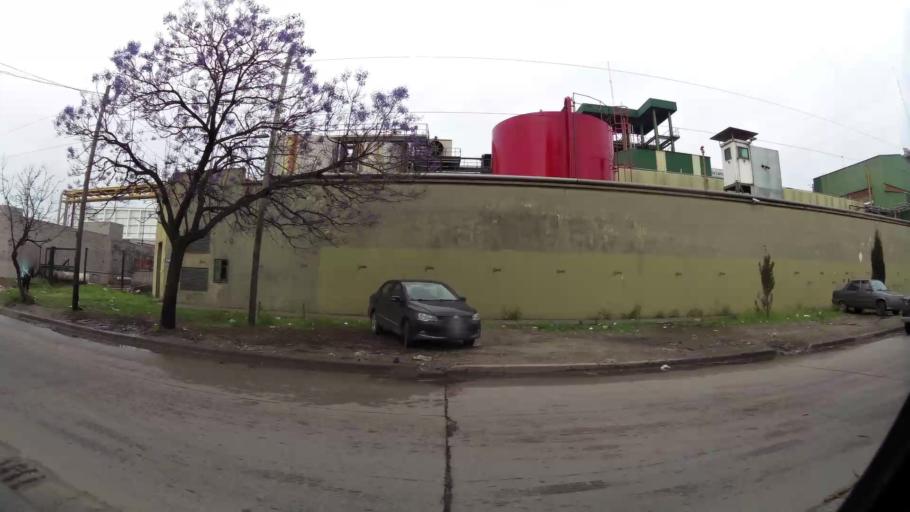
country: AR
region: Buenos Aires
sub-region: Partido de Lanus
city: Lanus
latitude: -34.7146
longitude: -58.3605
